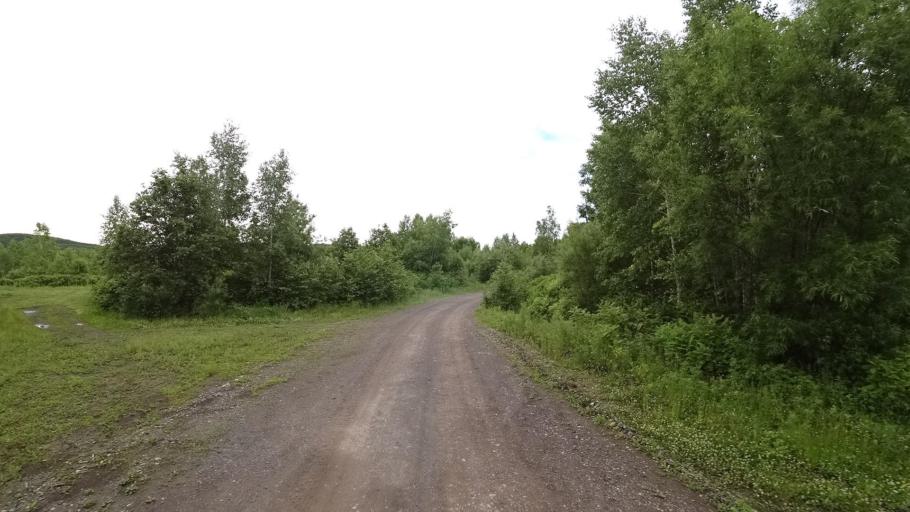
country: RU
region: Khabarovsk Krai
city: Amursk
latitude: 49.9121
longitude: 136.1581
